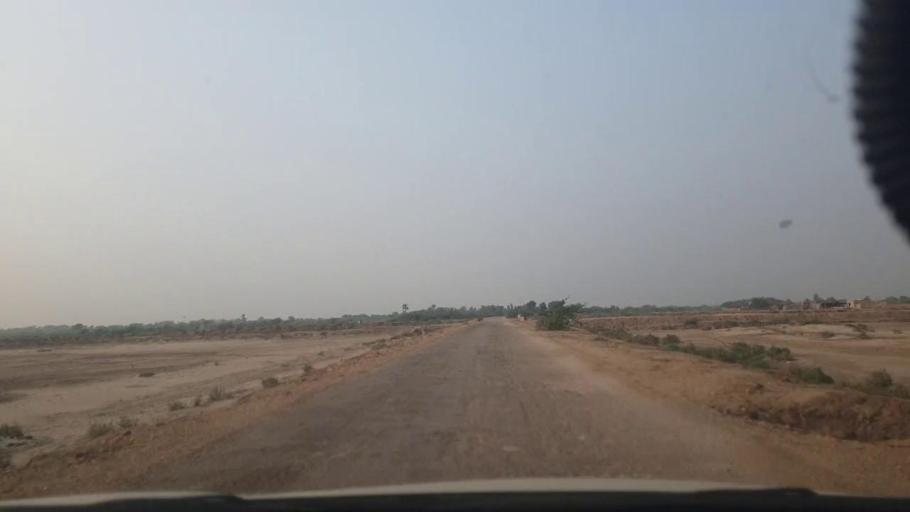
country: PK
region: Sindh
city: Bulri
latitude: 24.8200
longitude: 68.4044
